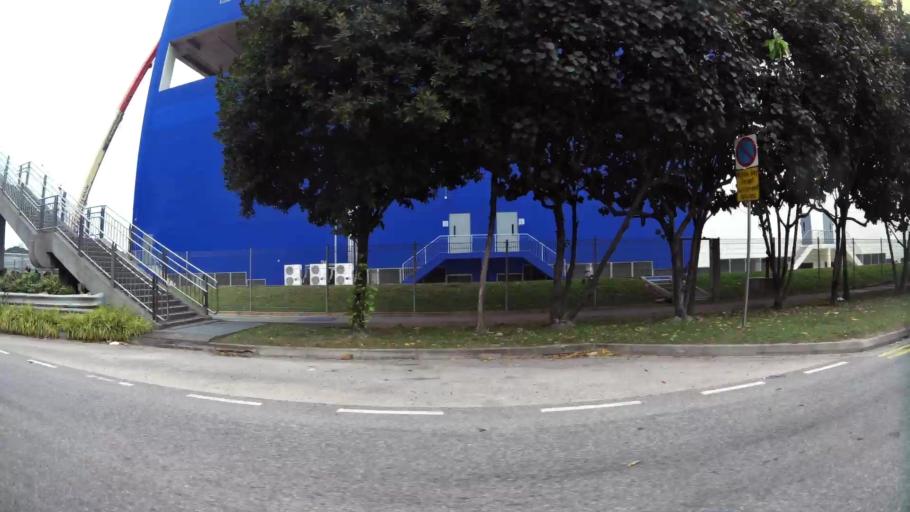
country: SG
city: Singapore
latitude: 1.3137
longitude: 103.7233
